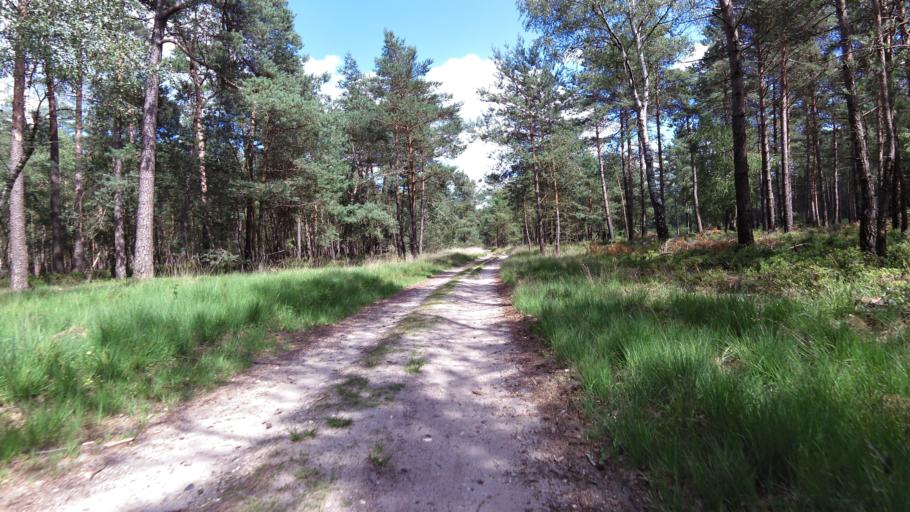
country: NL
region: Gelderland
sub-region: Gemeente Epe
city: Vaassen
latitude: 52.2594
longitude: 5.8801
